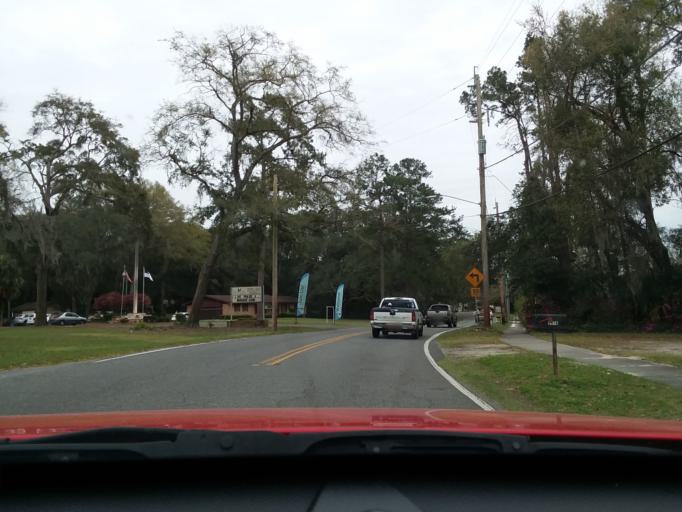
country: US
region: Florida
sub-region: Duval County
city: Jacksonville
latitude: 30.2935
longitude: -81.7438
